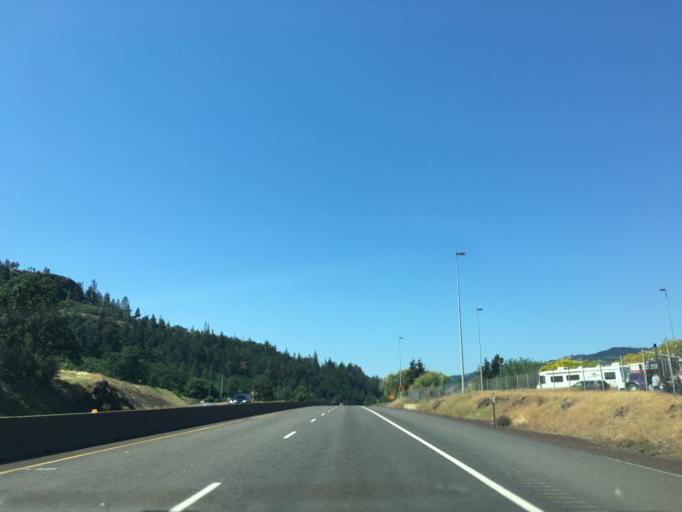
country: US
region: Oregon
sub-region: Wasco County
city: Chenoweth
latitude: 45.6953
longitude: -121.3382
